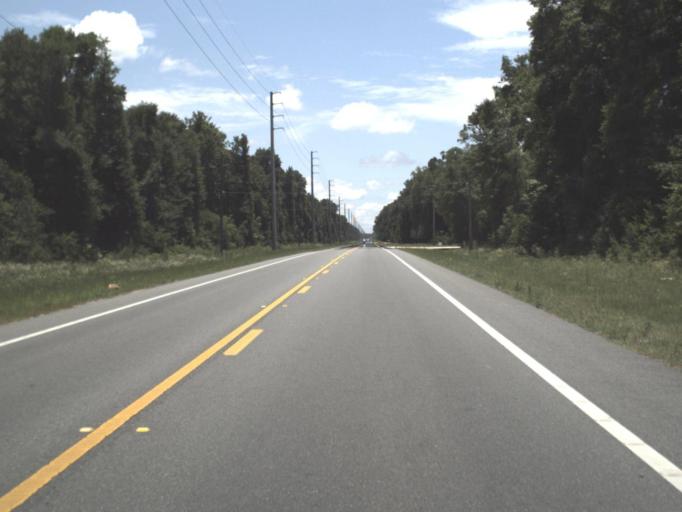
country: US
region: Florida
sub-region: Dixie County
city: Cross City
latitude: 29.6461
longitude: -82.9837
